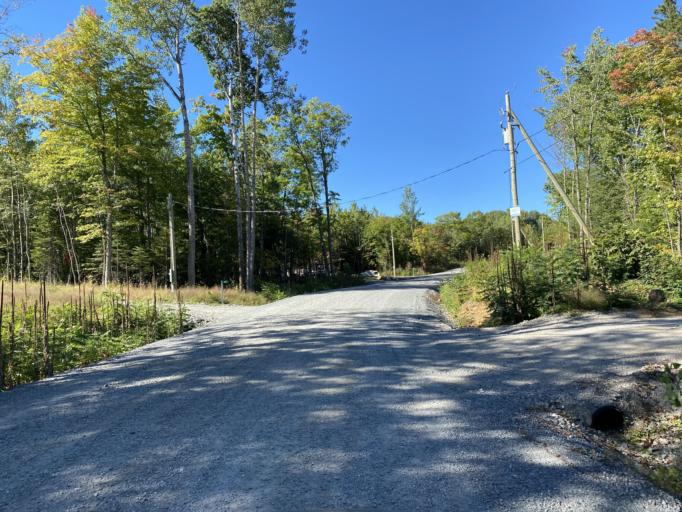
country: CA
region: Quebec
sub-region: Outaouais
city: Val-des-Monts
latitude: 45.5709
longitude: -75.5268
